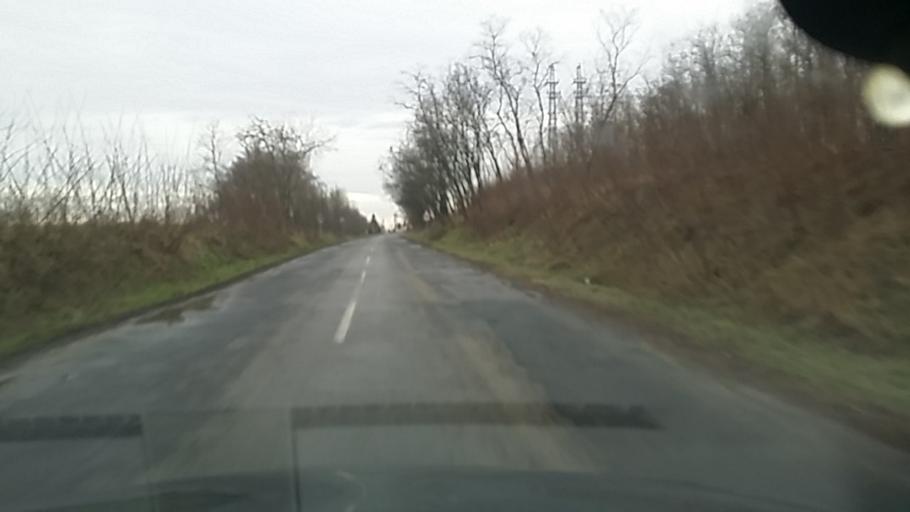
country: HU
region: Szabolcs-Szatmar-Bereg
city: Nyirbogdany
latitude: 48.0729
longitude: 21.8596
